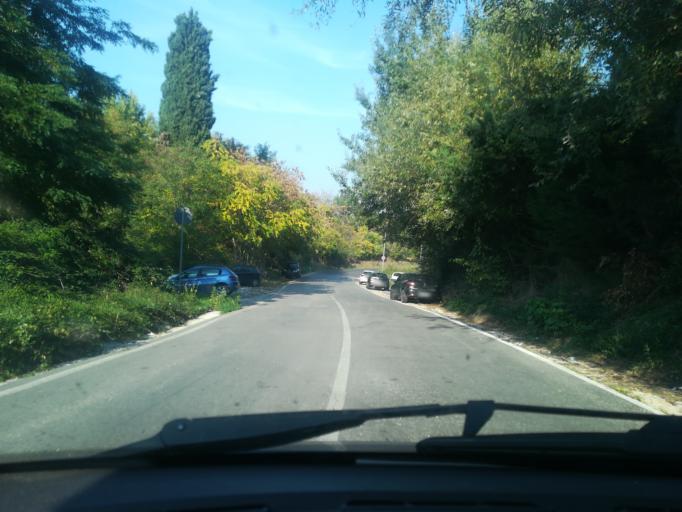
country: IT
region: The Marches
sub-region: Provincia di Macerata
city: Macerata
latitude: 43.3029
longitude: 13.4507
